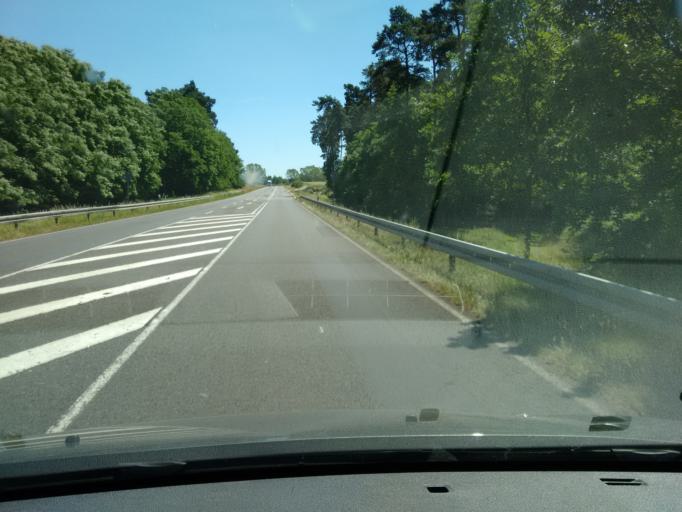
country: DE
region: Brandenburg
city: Beeskow
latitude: 52.1940
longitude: 14.2732
